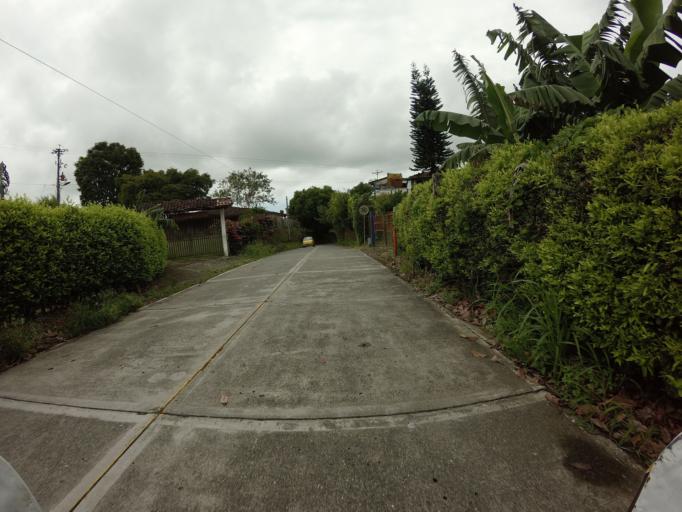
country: CO
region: Valle del Cauca
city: Ulloa
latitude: 4.6997
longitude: -75.7605
